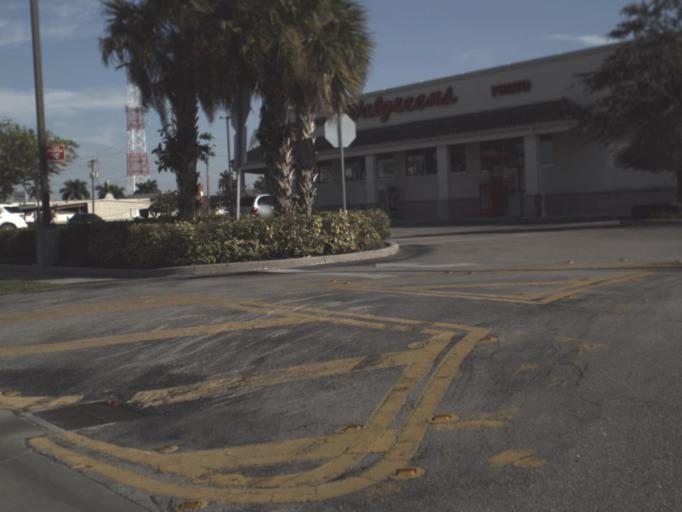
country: US
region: Florida
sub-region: Hendry County
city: Clewiston
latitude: 26.7541
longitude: -80.9371
